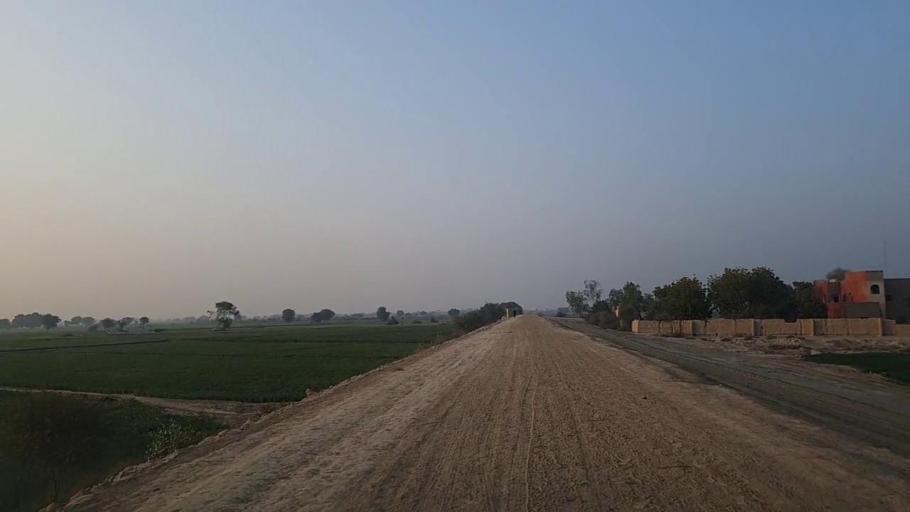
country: PK
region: Sindh
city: Sann
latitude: 26.1927
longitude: 68.0900
